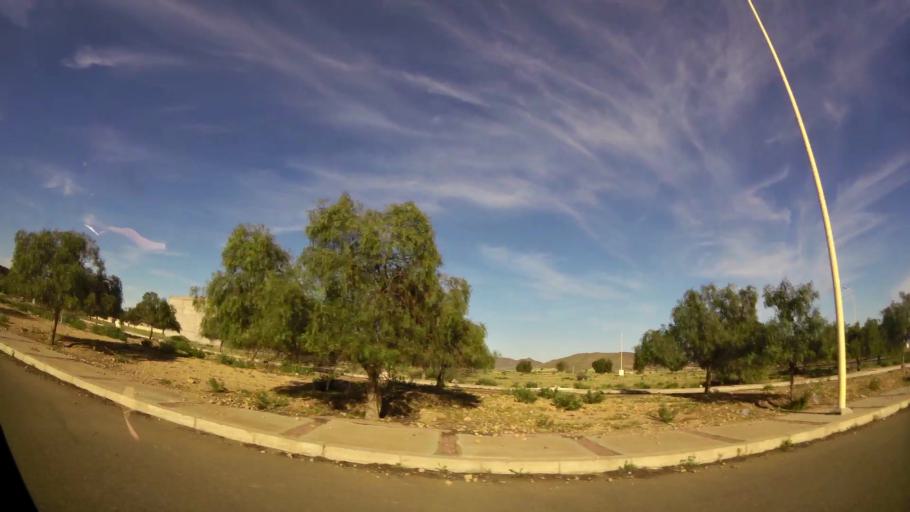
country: MA
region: Marrakech-Tensift-Al Haouz
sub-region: Marrakech
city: Marrakesh
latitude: 31.7573
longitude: -8.0946
